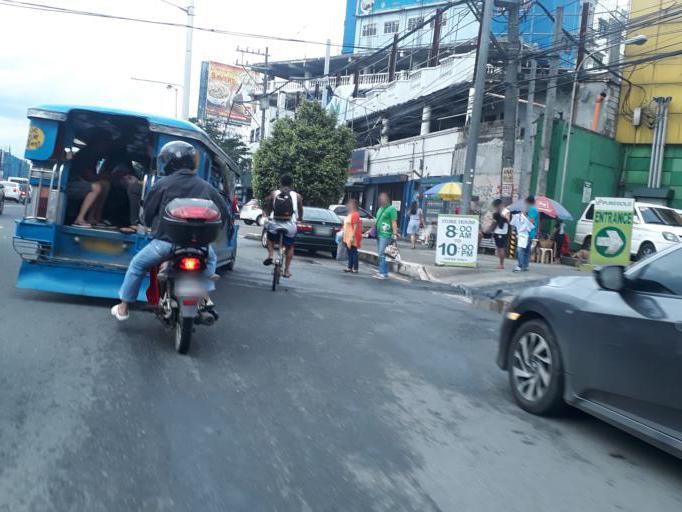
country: PH
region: Metro Manila
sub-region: Quezon City
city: Quezon City
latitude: 14.6749
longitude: 121.0818
